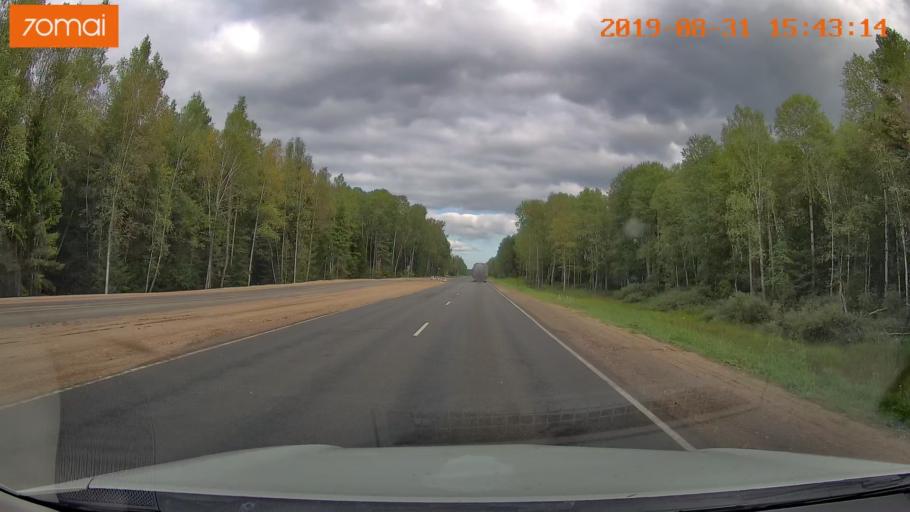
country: RU
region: Kaluga
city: Mosal'sk
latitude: 54.6518
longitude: 34.9063
